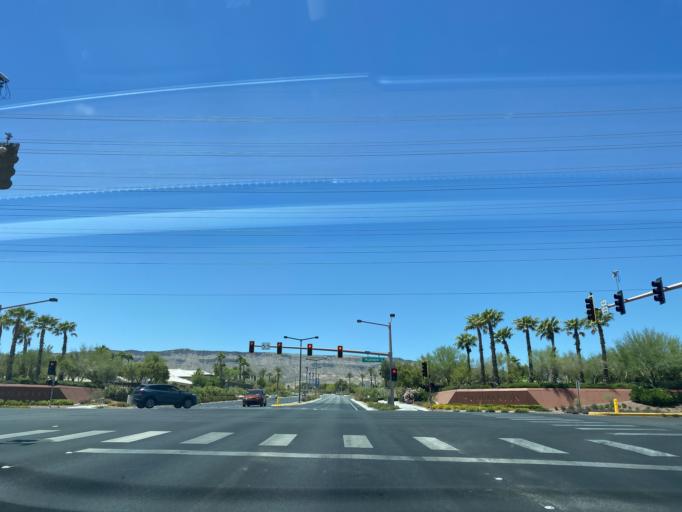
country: US
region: Nevada
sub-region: Clark County
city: Summerlin South
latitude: 36.1002
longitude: -115.3148
